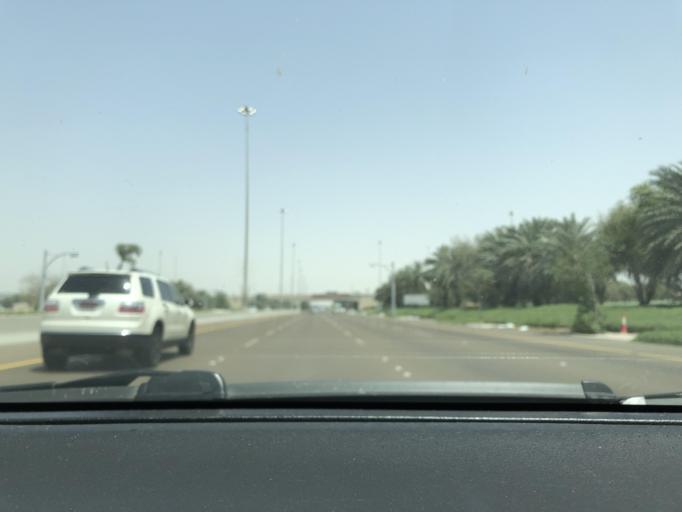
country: AE
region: Abu Dhabi
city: Abu Dhabi
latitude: 24.4160
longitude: 54.5003
